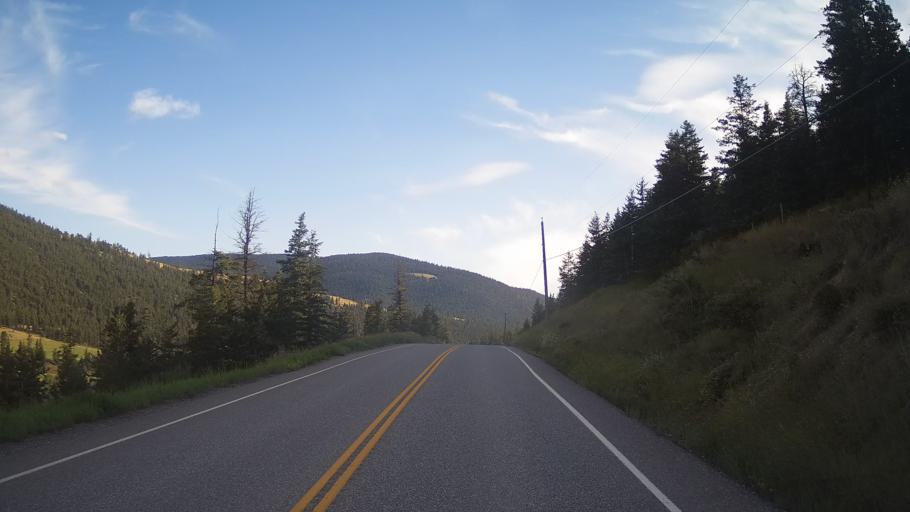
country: CA
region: British Columbia
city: Cache Creek
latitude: 50.8477
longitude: -121.5393
